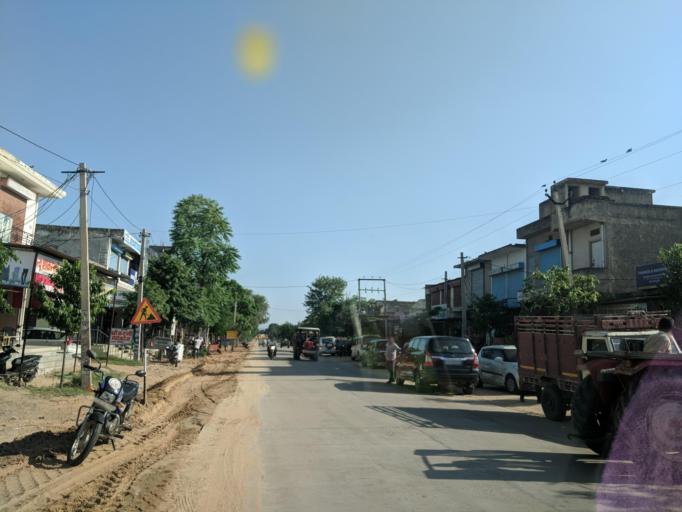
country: IN
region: Rajasthan
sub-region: Sikar
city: Losal
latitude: 27.4084
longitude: 75.0586
